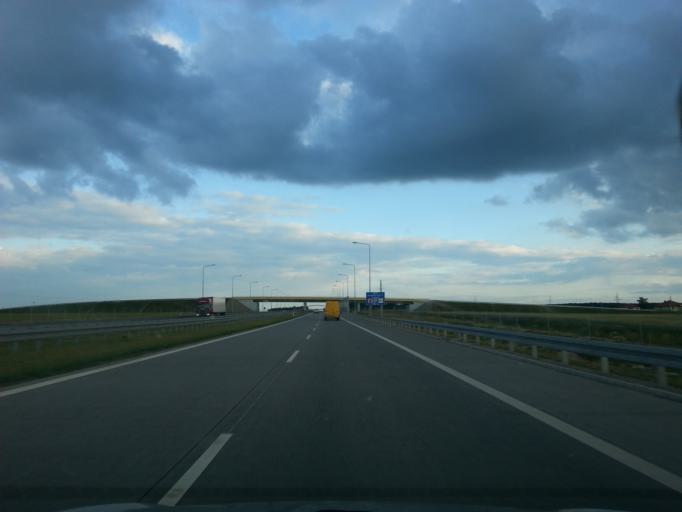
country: PL
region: Lodz Voivodeship
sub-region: Powiat sieradzki
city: Sieradz
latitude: 51.5352
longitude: 18.6963
